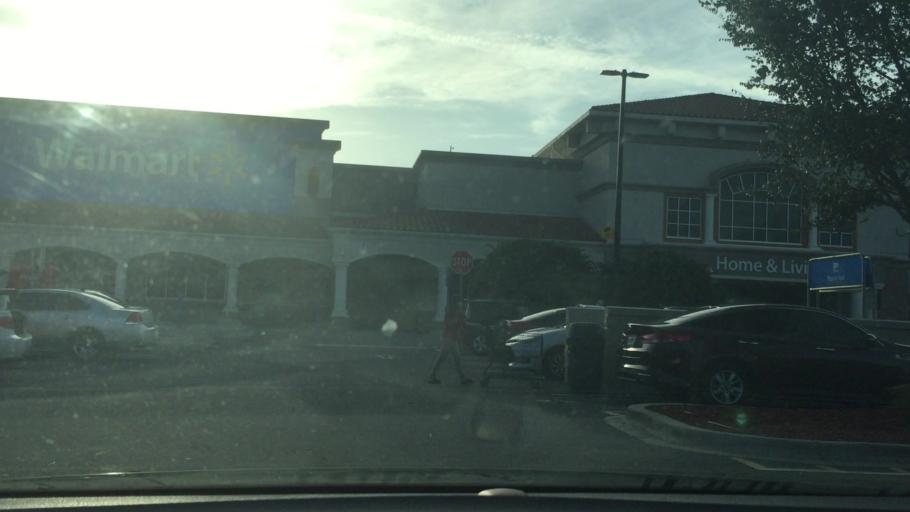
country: US
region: Florida
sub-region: Orange County
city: Fairview Shores
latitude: 28.5714
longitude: -81.4186
